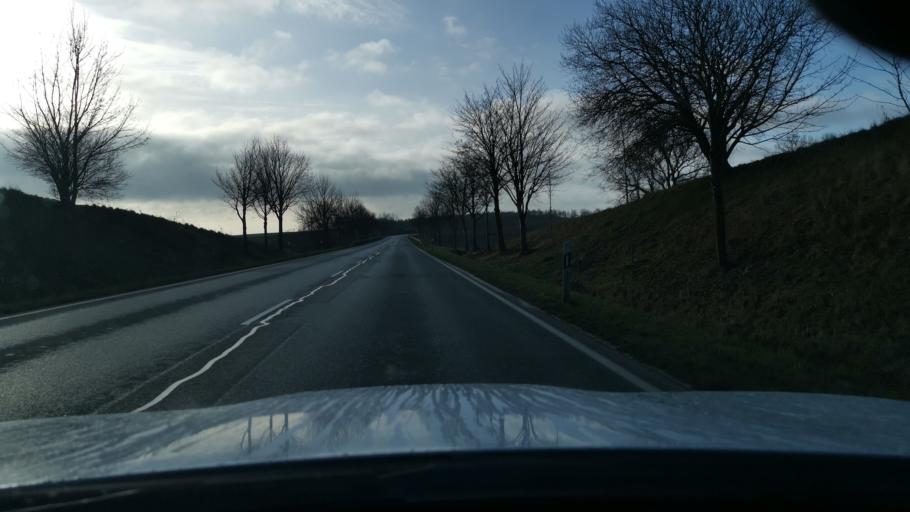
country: DE
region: Mecklenburg-Vorpommern
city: Laage
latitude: 53.9203
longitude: 12.3155
